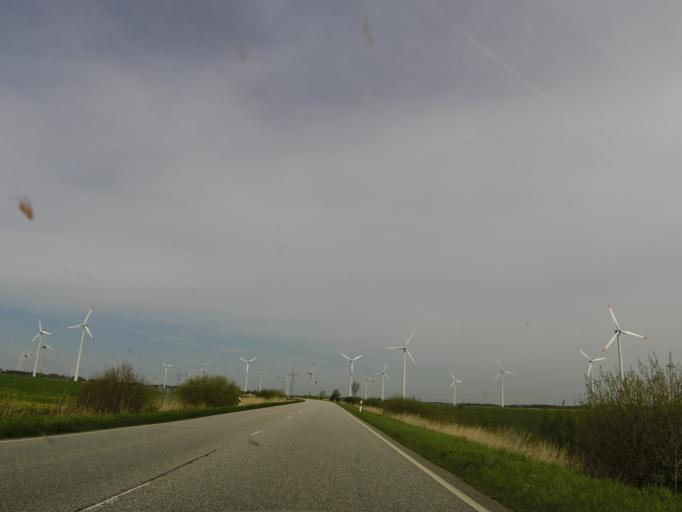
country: DE
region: Schleswig-Holstein
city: Stelle-Wittenwurth
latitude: 54.2575
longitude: 9.0361
